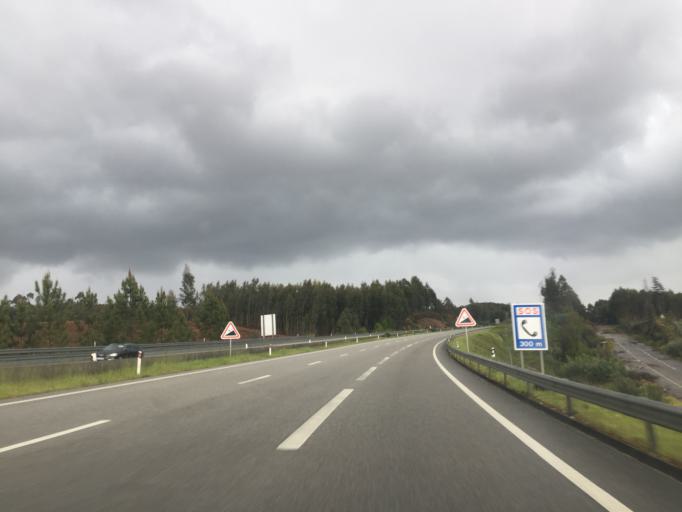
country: PT
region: Aveiro
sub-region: Agueda
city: Valongo
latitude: 40.6659
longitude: -8.3990
